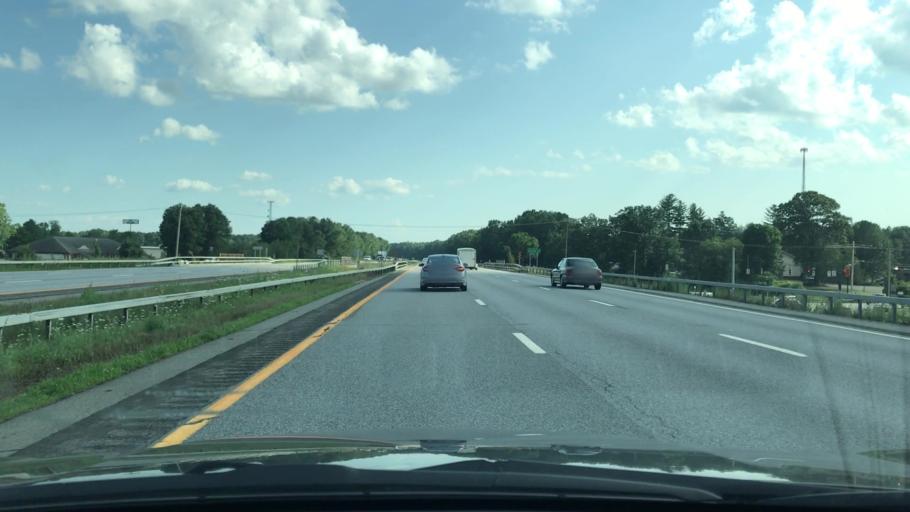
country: US
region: New York
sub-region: Warren County
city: West Glens Falls
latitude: 43.2987
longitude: -73.6789
